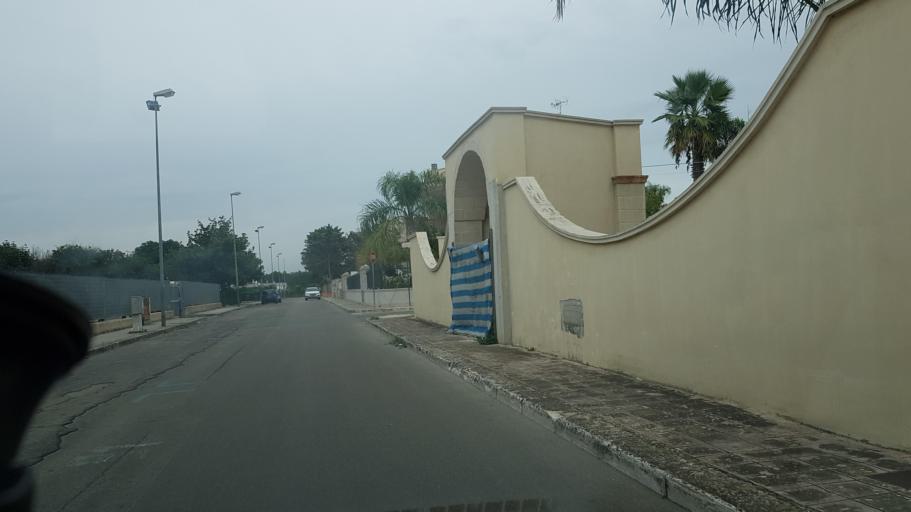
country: IT
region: Apulia
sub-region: Provincia di Brindisi
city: Cellino San Marco
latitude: 40.4747
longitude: 17.9703
